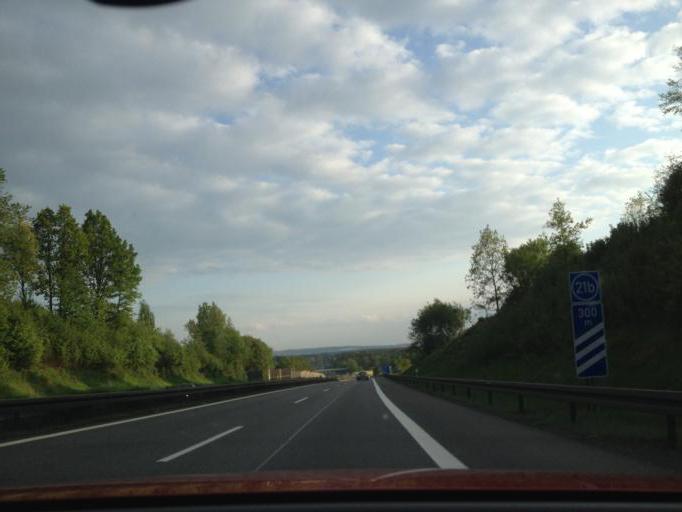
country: DE
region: Bavaria
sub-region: Upper Palatinate
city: Neustadt an der Waldnaab
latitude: 49.7273
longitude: 12.1555
